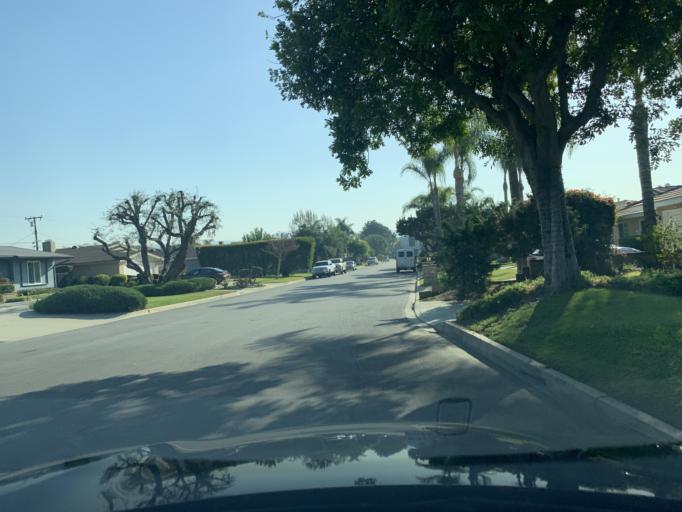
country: US
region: California
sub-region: Los Angeles County
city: Covina
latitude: 34.0778
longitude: -117.8951
